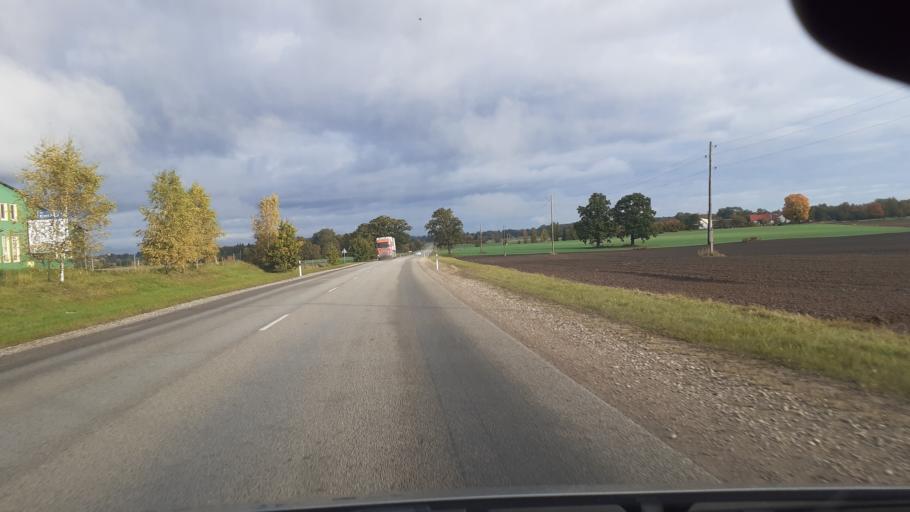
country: LV
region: Kuldigas Rajons
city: Kuldiga
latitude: 56.9723
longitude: 21.9323
